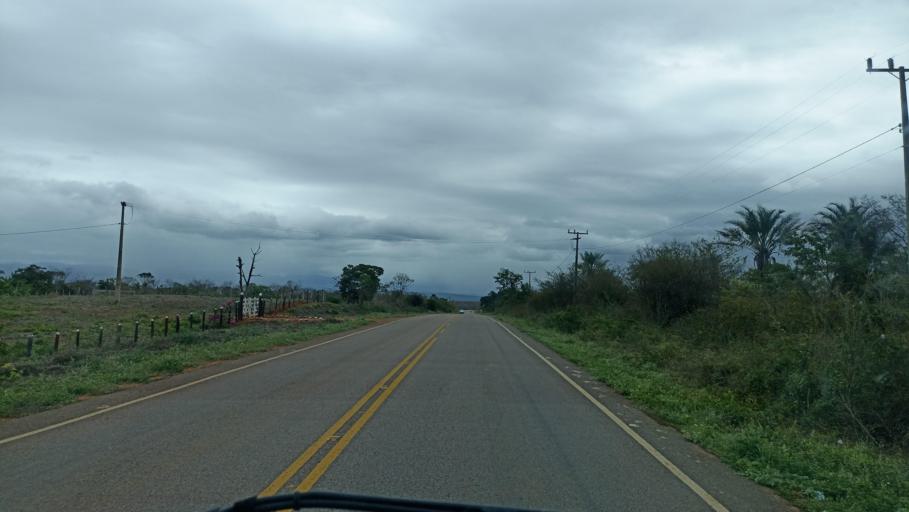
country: BR
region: Bahia
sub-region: Andarai
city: Vera Cruz
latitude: -12.9896
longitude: -41.0036
